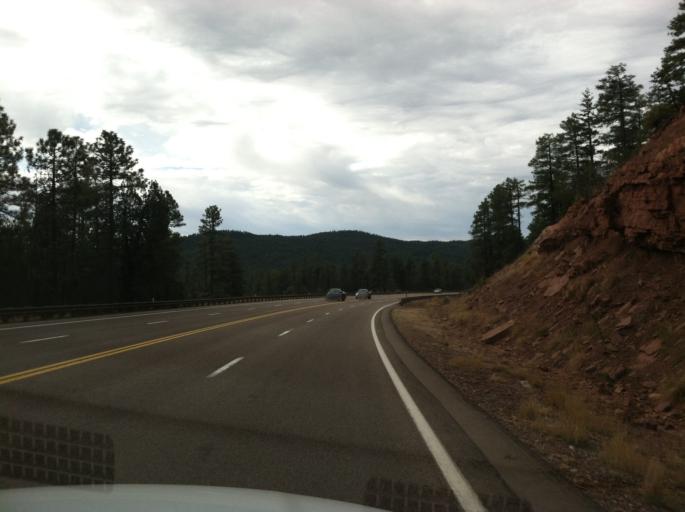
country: US
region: Arizona
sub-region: Gila County
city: Star Valley
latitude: 34.3034
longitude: -110.9547
